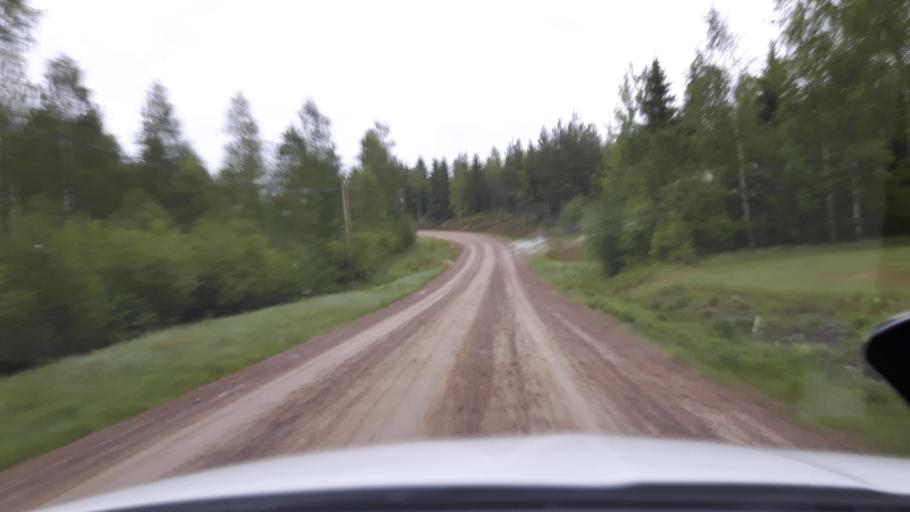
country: SE
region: Vaesternorrland
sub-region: Ange Kommun
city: Ange
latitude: 62.1793
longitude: 15.6323
